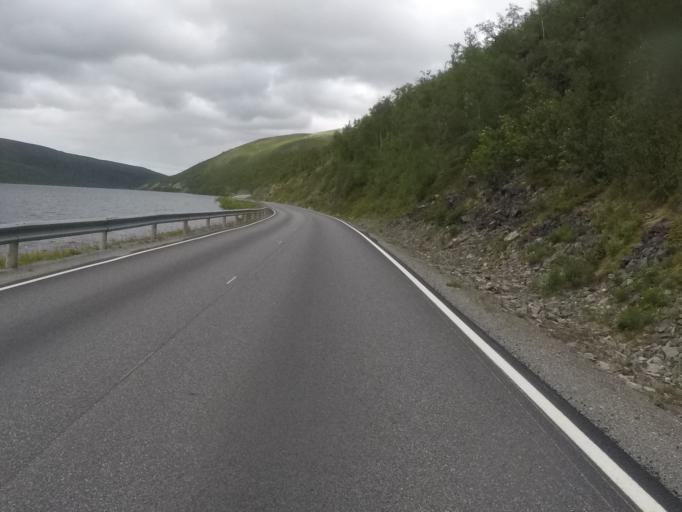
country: NO
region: Finnmark Fylke
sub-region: Alta
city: Alta
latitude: 69.6854
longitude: 23.4278
